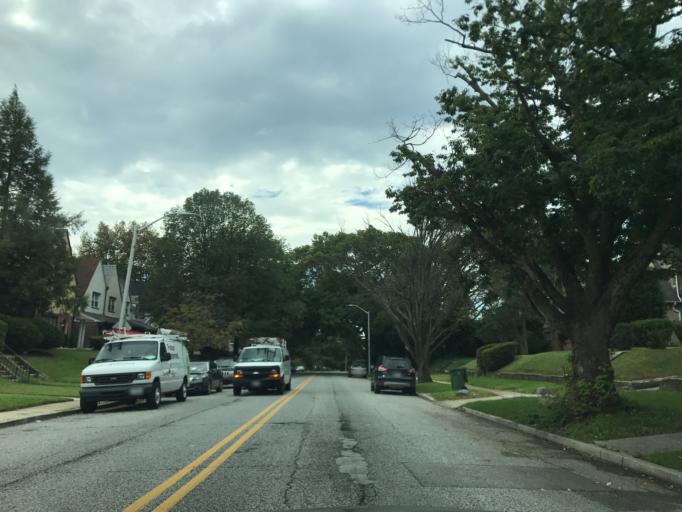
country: US
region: Maryland
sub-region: Baltimore County
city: Lochearn
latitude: 39.3254
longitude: -76.6652
